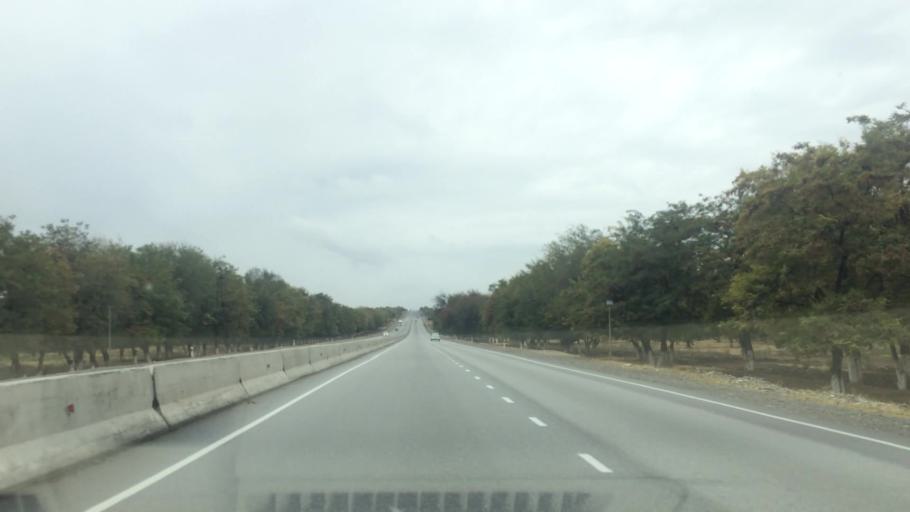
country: UZ
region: Samarqand
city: Bulung'ur
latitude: 39.8717
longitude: 67.4788
